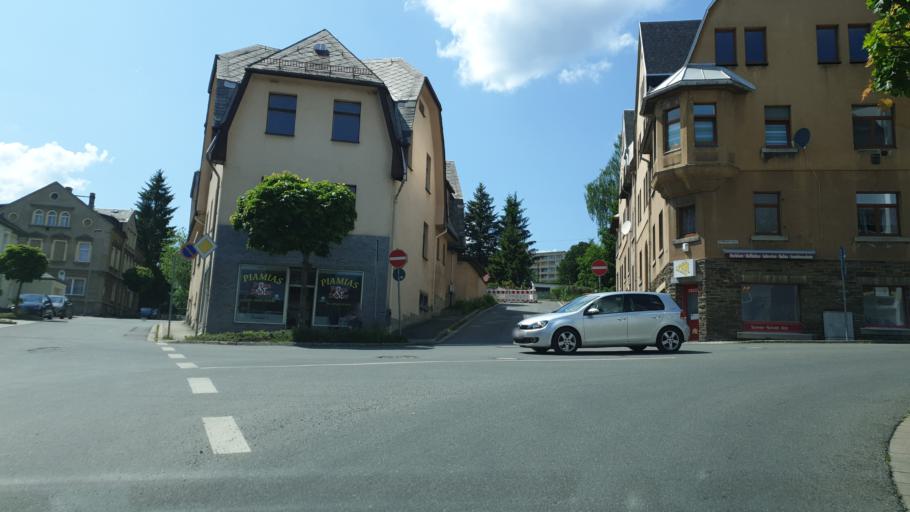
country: DE
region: Saxony
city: Klingenthal
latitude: 50.3581
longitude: 12.4580
